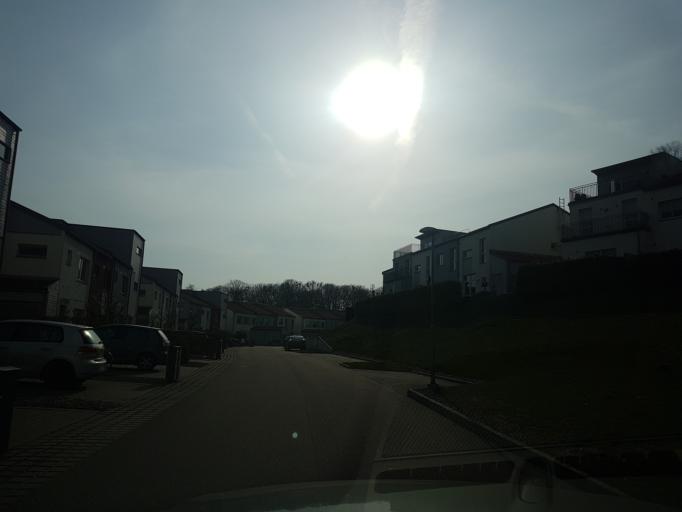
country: SE
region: Skane
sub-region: Ystads Kommun
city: Ystad
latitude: 55.4385
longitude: 13.8290
